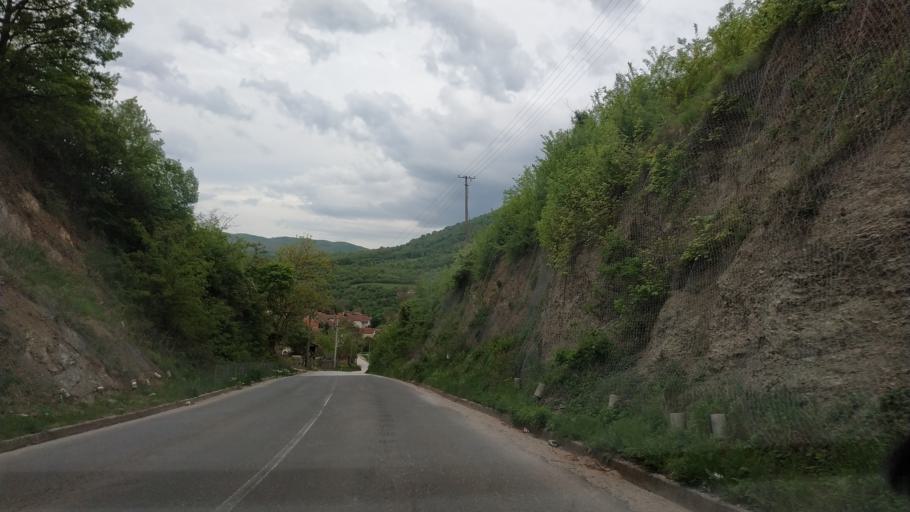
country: RS
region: Central Serbia
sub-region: Nisavski Okrug
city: Aleksinac
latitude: 43.6384
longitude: 21.7140
